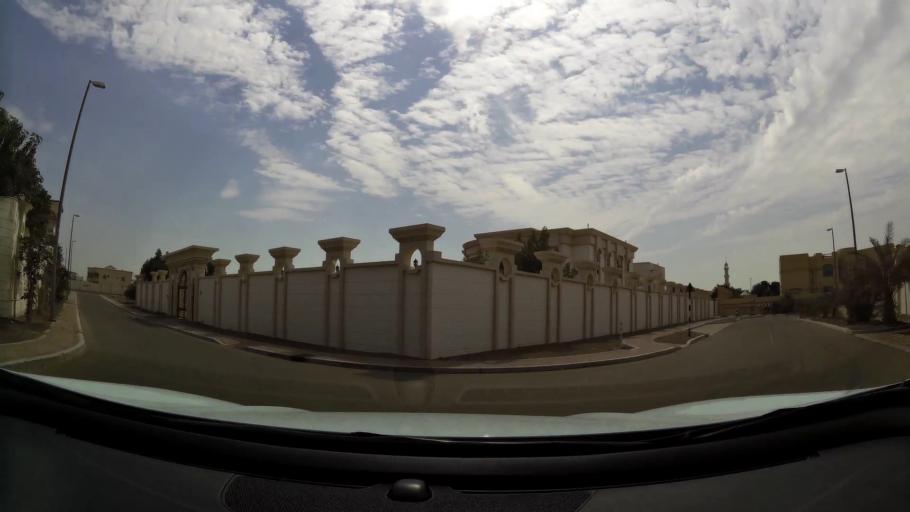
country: AE
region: Abu Dhabi
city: Al Ain
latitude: 24.1933
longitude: 55.8057
